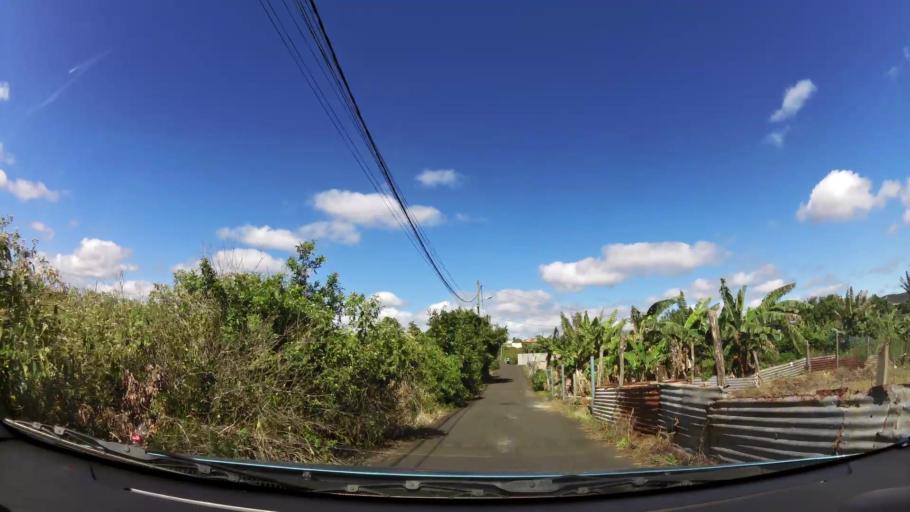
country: MU
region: Plaines Wilhems
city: Vacoas
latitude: -20.3093
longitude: 57.4751
